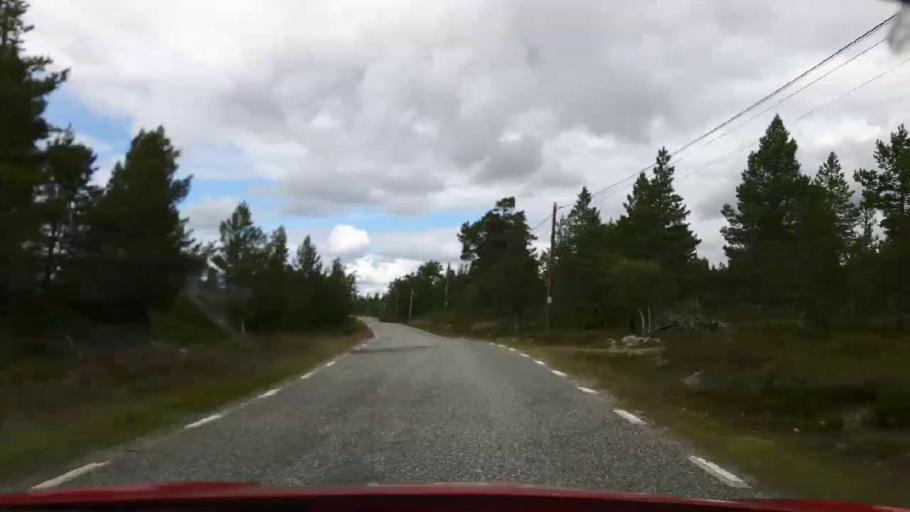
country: NO
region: Hedmark
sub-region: Engerdal
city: Engerdal
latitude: 62.3287
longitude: 12.8081
